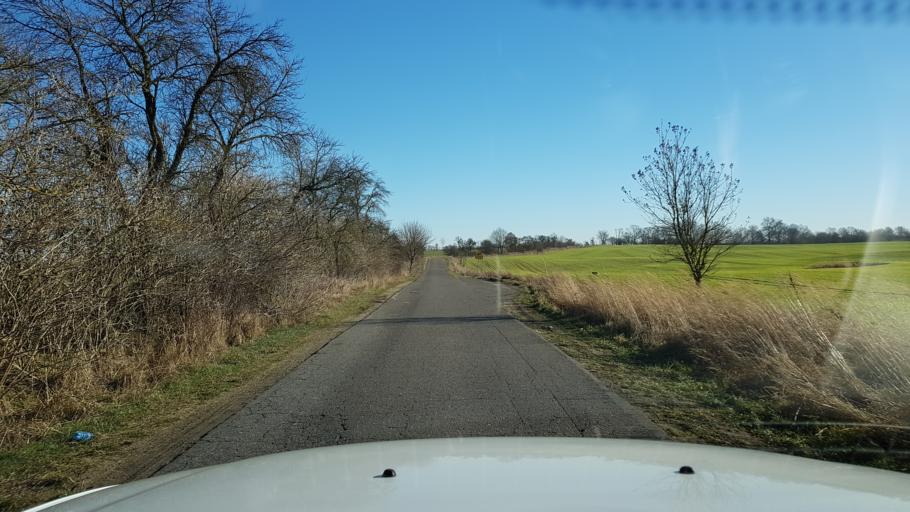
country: PL
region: West Pomeranian Voivodeship
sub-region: Powiat mysliborski
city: Barlinek
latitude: 53.0188
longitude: 15.1281
